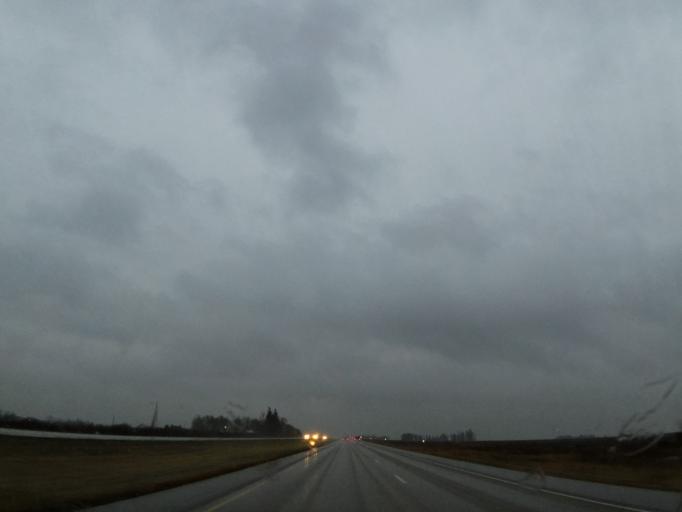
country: US
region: Iowa
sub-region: Worth County
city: Manly
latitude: 43.3420
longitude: -93.3487
